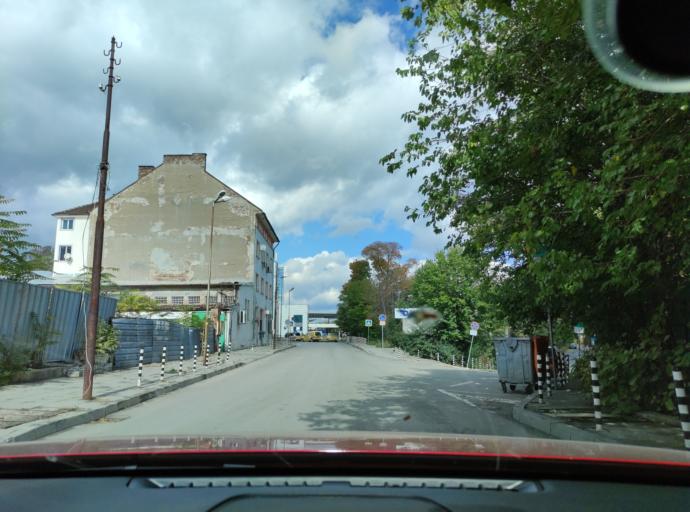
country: BG
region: Sofia-Capital
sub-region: Stolichna Obshtina
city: Sofia
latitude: 42.7086
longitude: 23.3242
